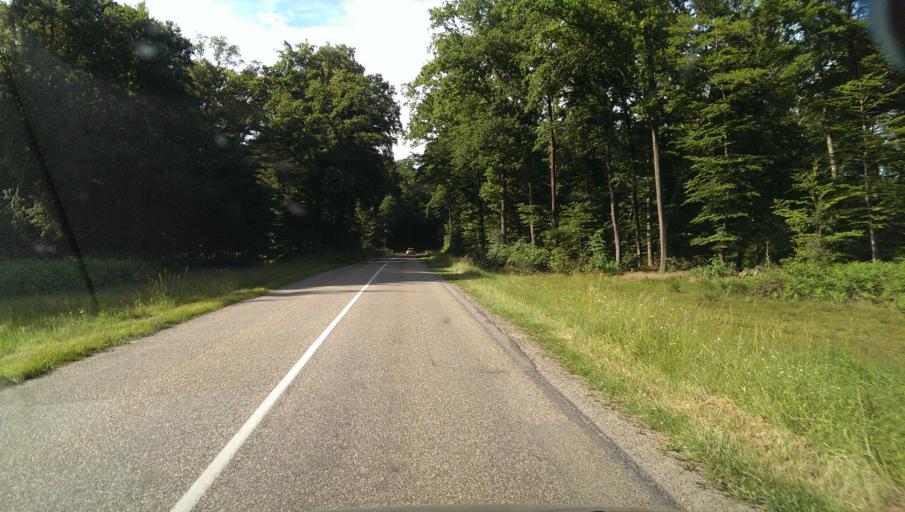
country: FR
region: Alsace
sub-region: Departement du Bas-Rhin
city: Roppenheim
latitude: 48.8862
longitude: 8.0424
